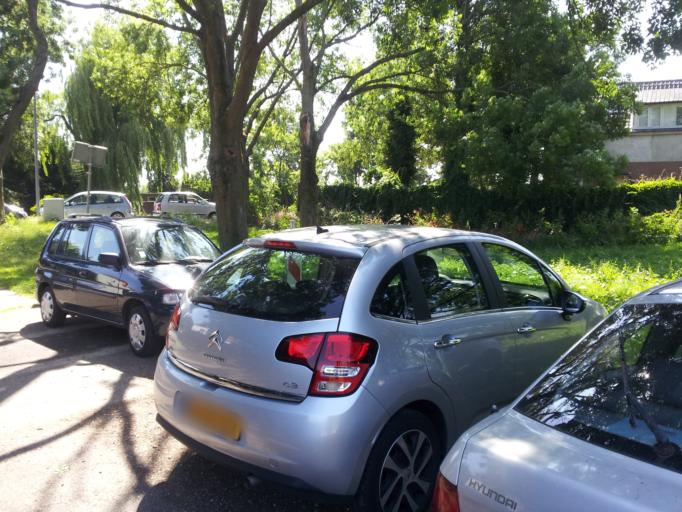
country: NL
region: South Holland
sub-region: Gemeente Rotterdam
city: Rotterdam
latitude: 51.9402
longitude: 4.4536
